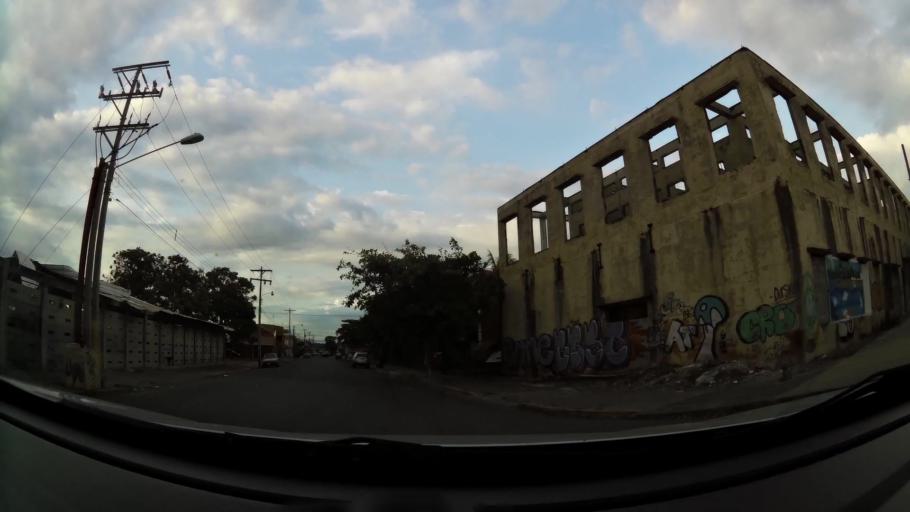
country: CR
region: Puntarenas
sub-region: Canton Central de Puntarenas
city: Puntarenas
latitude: 9.9762
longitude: -84.8293
